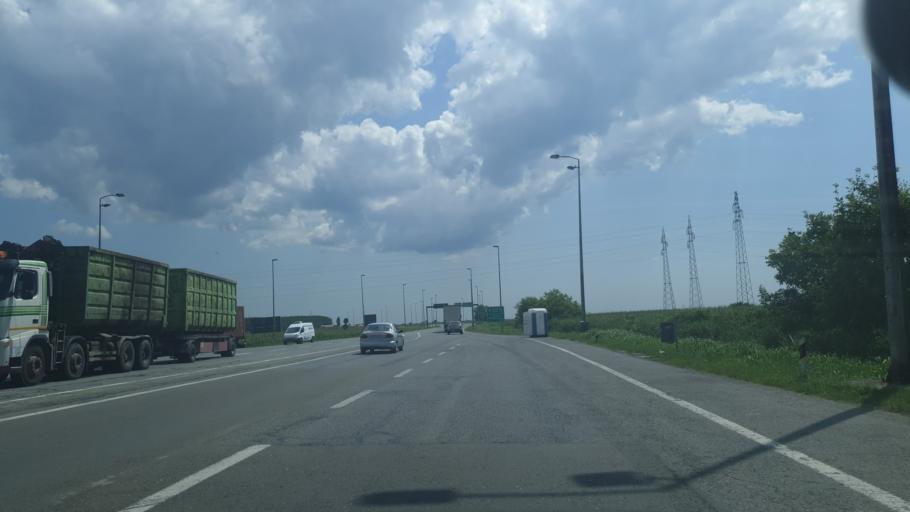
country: RS
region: Autonomna Pokrajina Vojvodina
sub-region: Sremski Okrug
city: Sremska Mitrovica
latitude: 44.9953
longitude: 19.6456
